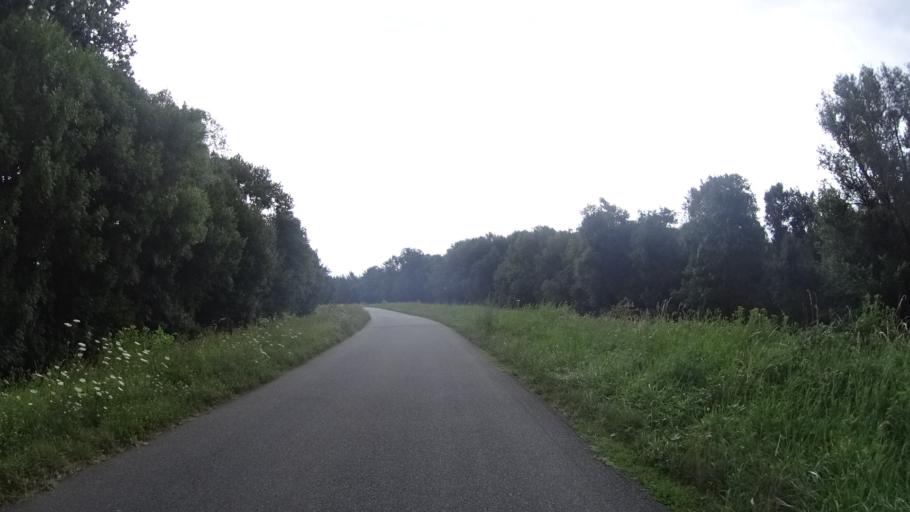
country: FR
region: Centre
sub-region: Departement du Loiret
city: Mareau-aux-Pres
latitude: 47.8624
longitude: 1.7997
